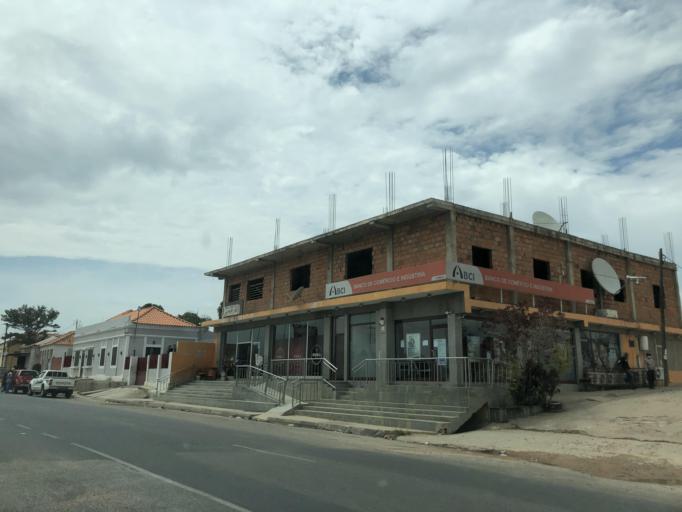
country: AO
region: Huila
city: Lubango
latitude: -14.9259
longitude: 13.5515
